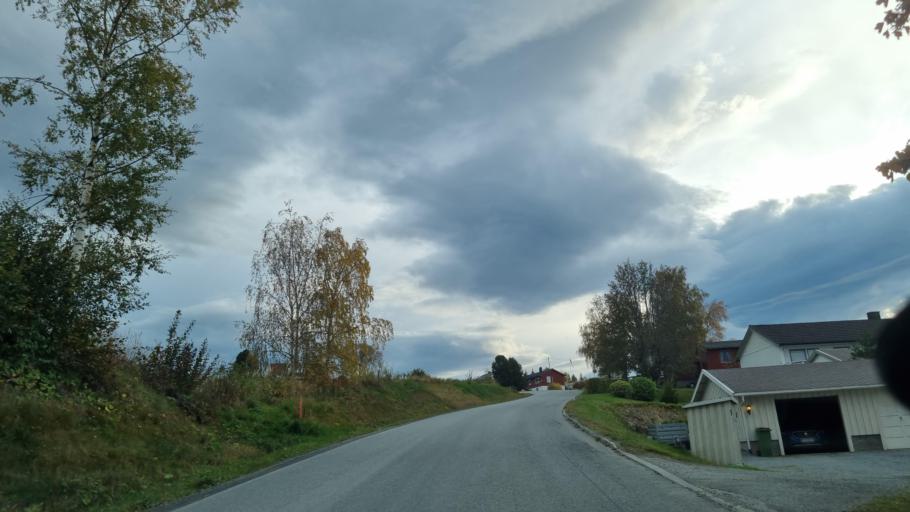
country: NO
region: Sor-Trondelag
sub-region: Malvik
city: Malvik
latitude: 63.4285
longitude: 10.7008
